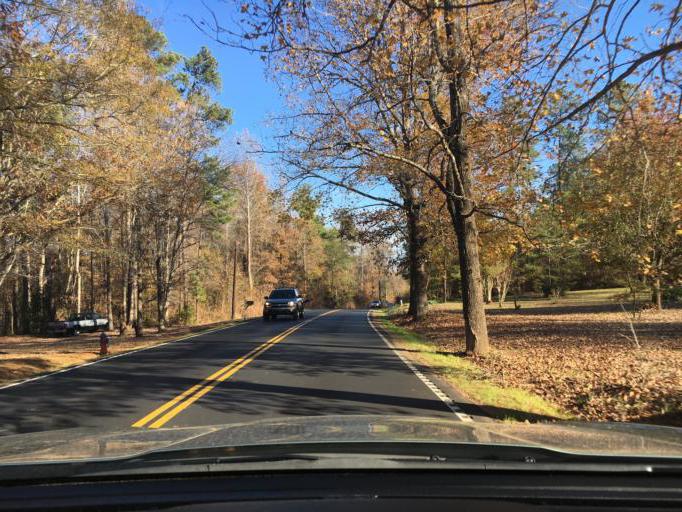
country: US
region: South Carolina
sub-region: Spartanburg County
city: Southern Shops
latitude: 34.9964
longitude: -82.0495
